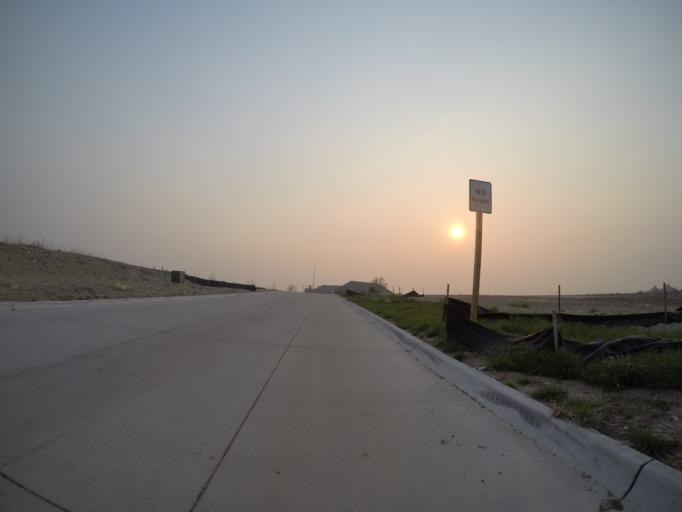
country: US
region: Kansas
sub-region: Riley County
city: Manhattan
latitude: 39.2135
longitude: -96.6385
